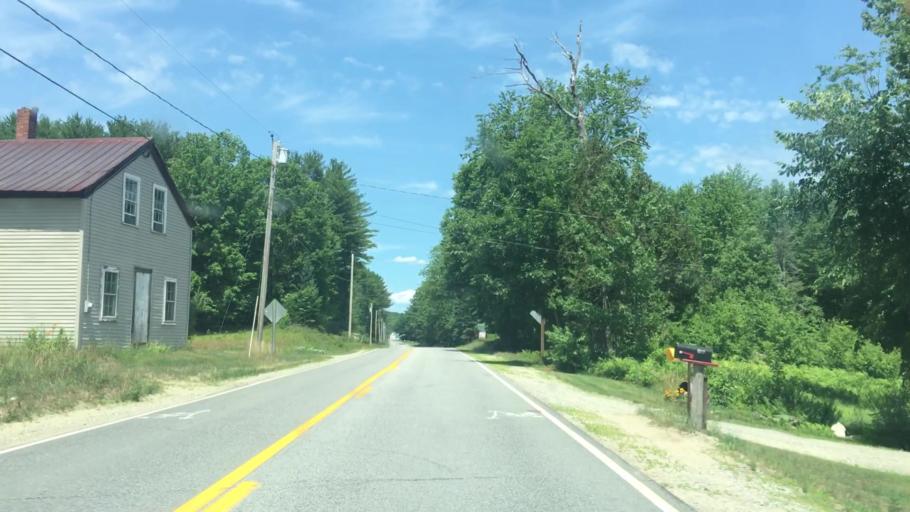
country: US
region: Maine
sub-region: Androscoggin County
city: Livermore
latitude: 44.3439
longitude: -70.1906
